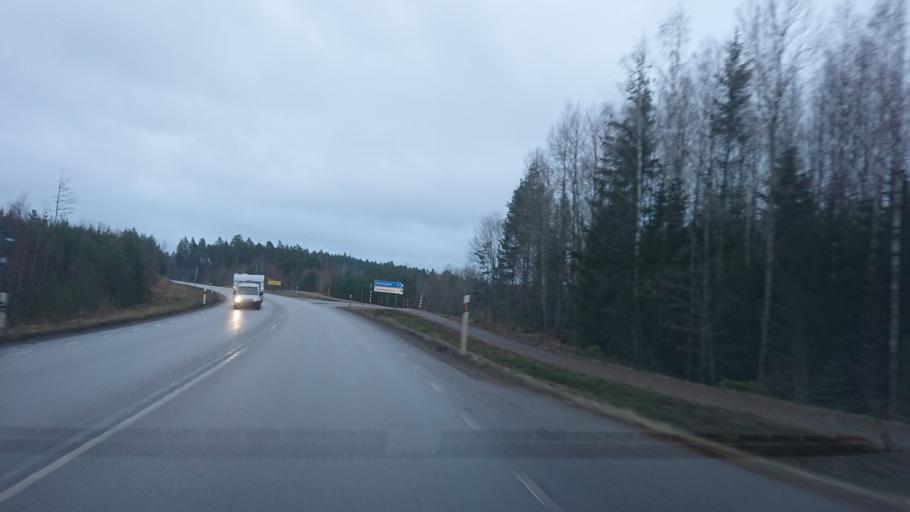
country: SE
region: Uppsala
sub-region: Osthammars Kommun
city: Bjorklinge
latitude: 60.0111
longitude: 17.5901
